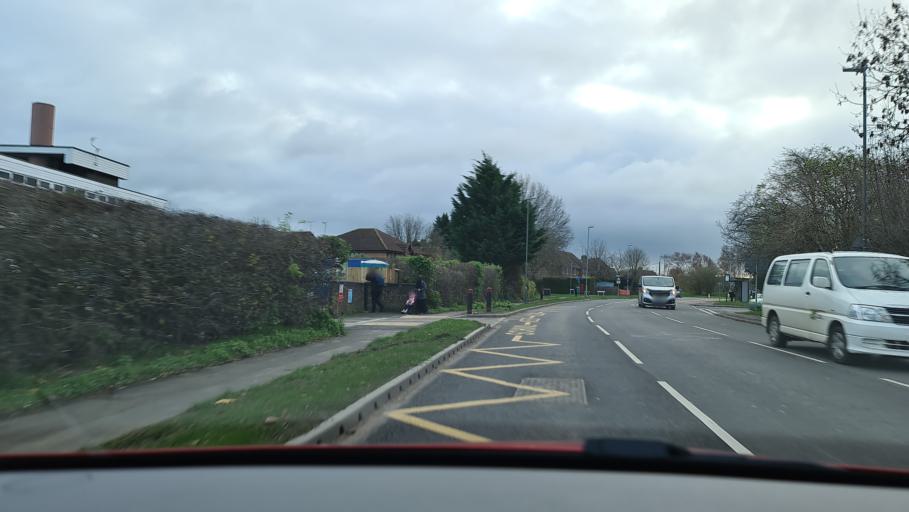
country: GB
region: England
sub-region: Buckinghamshire
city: Aylesbury
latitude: 51.8117
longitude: -0.8257
